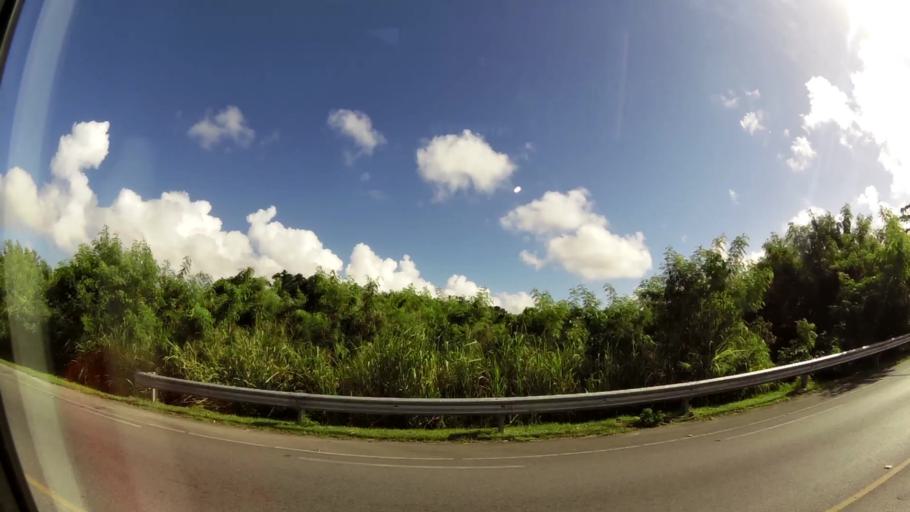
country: BB
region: Saint James
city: Holetown
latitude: 13.2013
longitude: -59.6165
